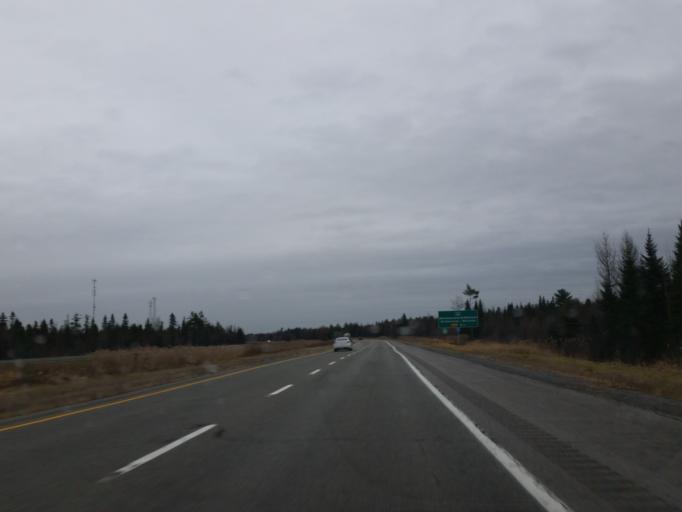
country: CA
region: Quebec
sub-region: Mauricie
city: Becancour
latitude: 46.4937
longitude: -72.3101
